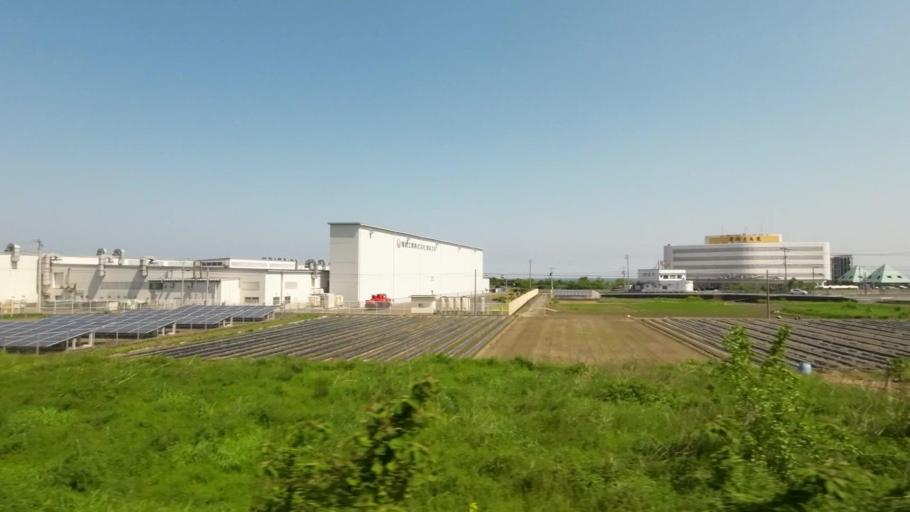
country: JP
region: Ehime
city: Kawanoecho
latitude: 33.9699
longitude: 133.4745
